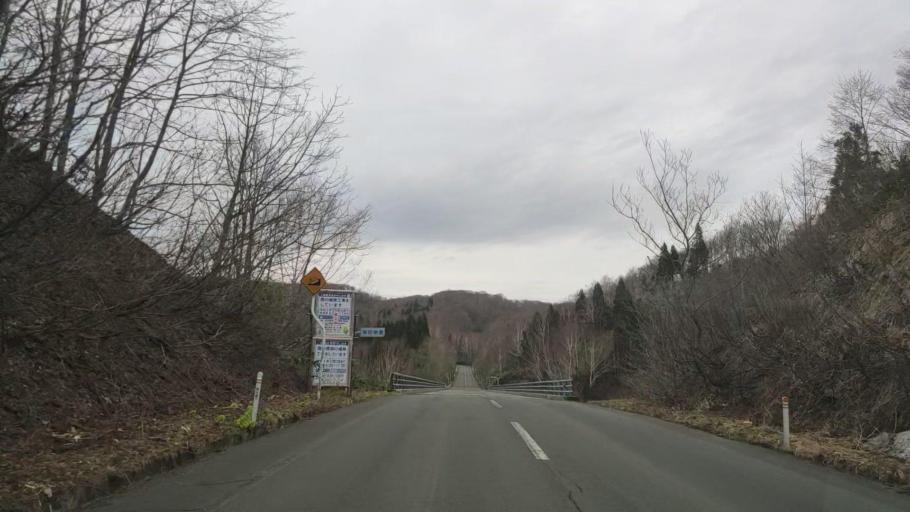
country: JP
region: Akita
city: Hanawa
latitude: 40.4127
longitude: 140.8463
